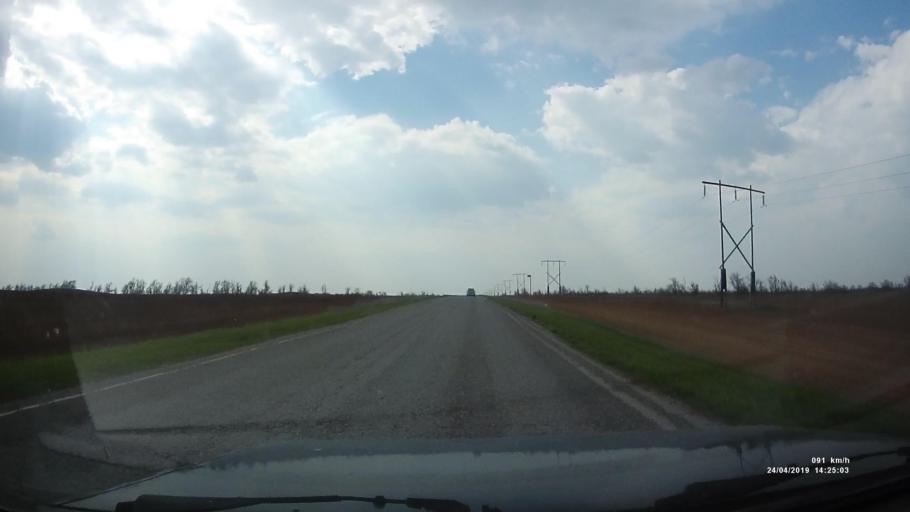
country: RU
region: Kalmykiya
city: Arshan'
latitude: 46.3298
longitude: 44.0862
